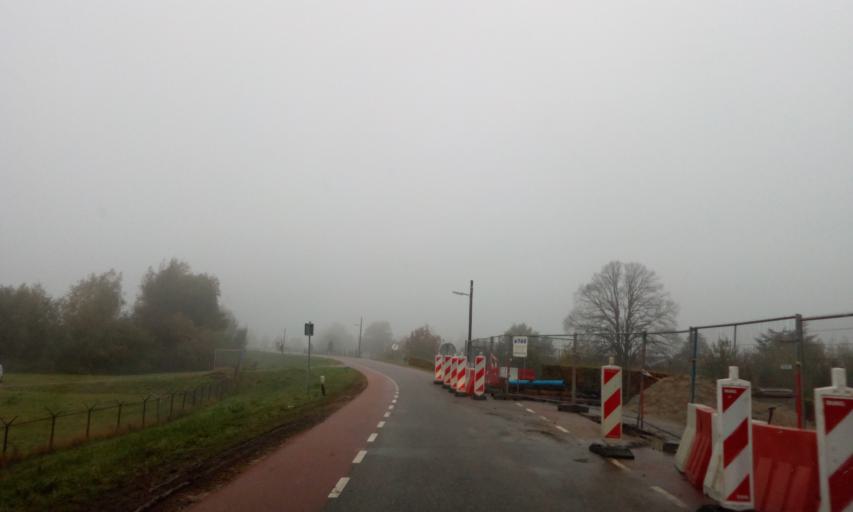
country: NL
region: South Holland
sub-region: Molenwaard
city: Liesveld
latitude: 51.9189
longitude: 4.7725
